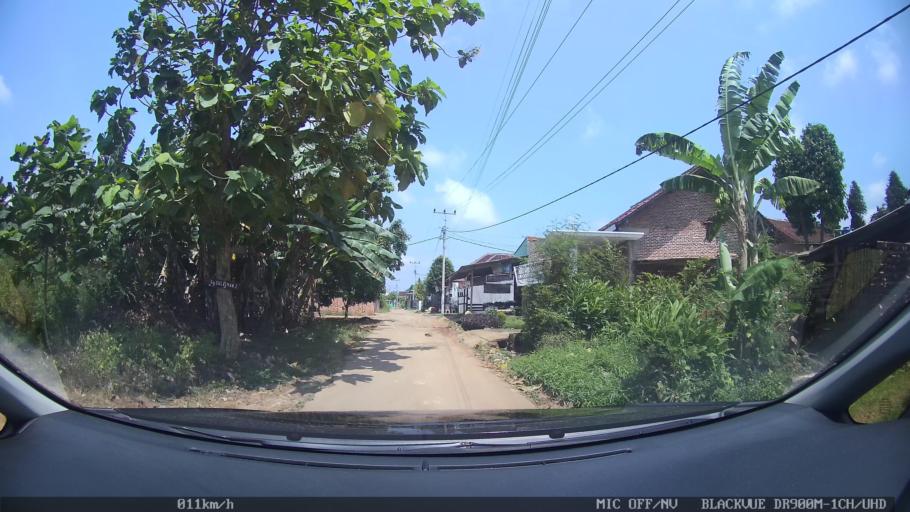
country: ID
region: Lampung
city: Kedaton
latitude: -5.3541
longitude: 105.2786
